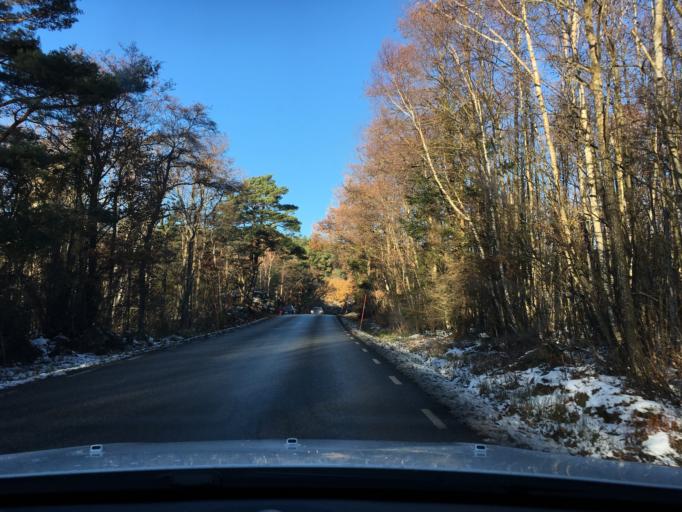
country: SE
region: Vaestra Goetaland
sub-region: Tjorns Kommun
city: Myggenas
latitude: 58.0627
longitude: 11.6821
